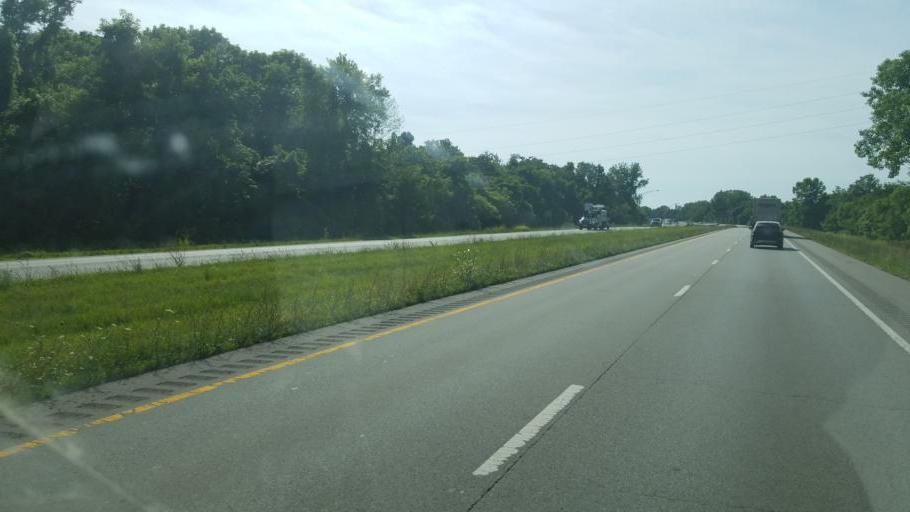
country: US
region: Ohio
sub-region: Hocking County
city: Logan
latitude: 39.5326
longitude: -82.3970
